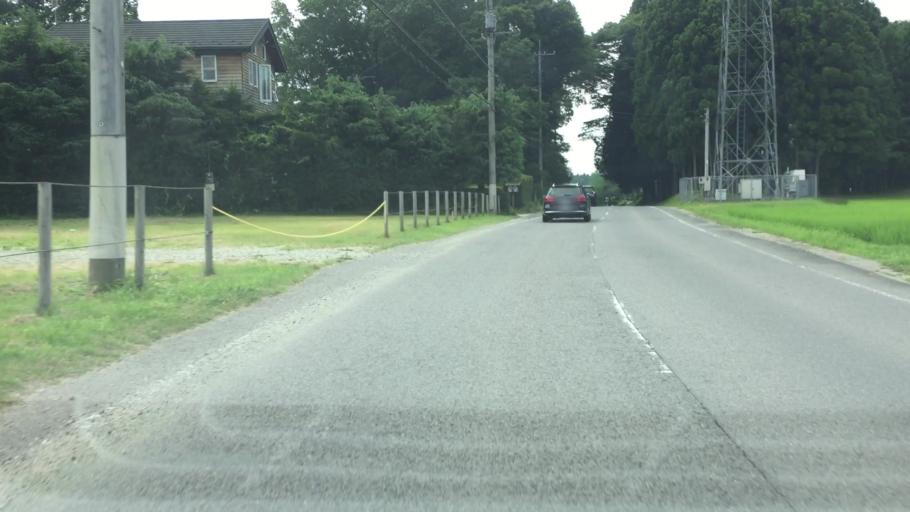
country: JP
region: Tochigi
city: Kuroiso
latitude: 37.0469
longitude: 140.0415
